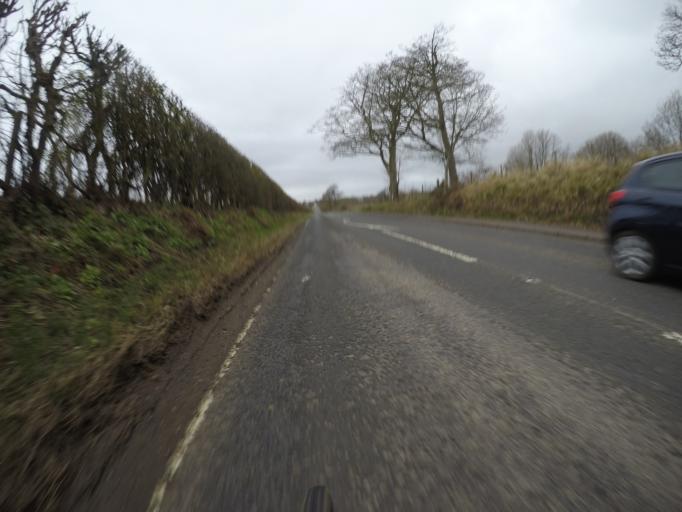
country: GB
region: Scotland
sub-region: North Ayrshire
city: Springside
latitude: 55.6118
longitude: -4.5779
